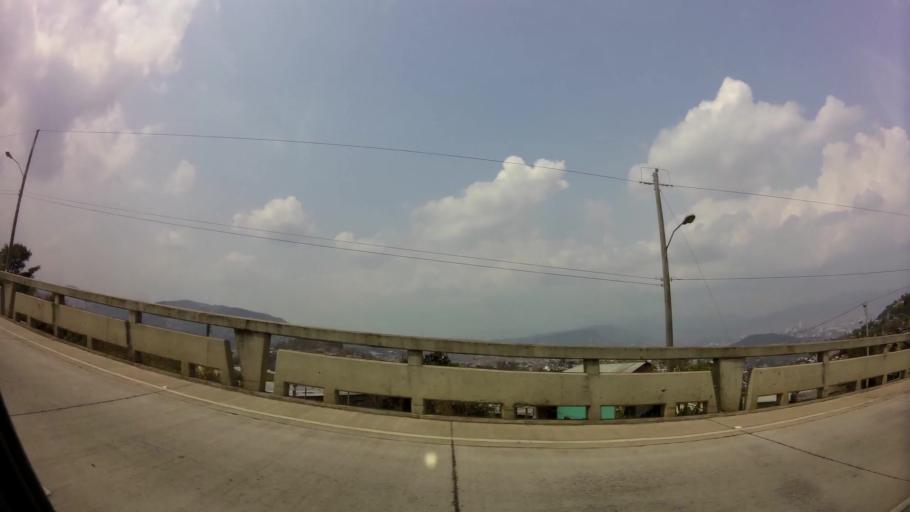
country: HN
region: Francisco Morazan
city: Tegucigalpa
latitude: 14.0830
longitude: -87.2397
